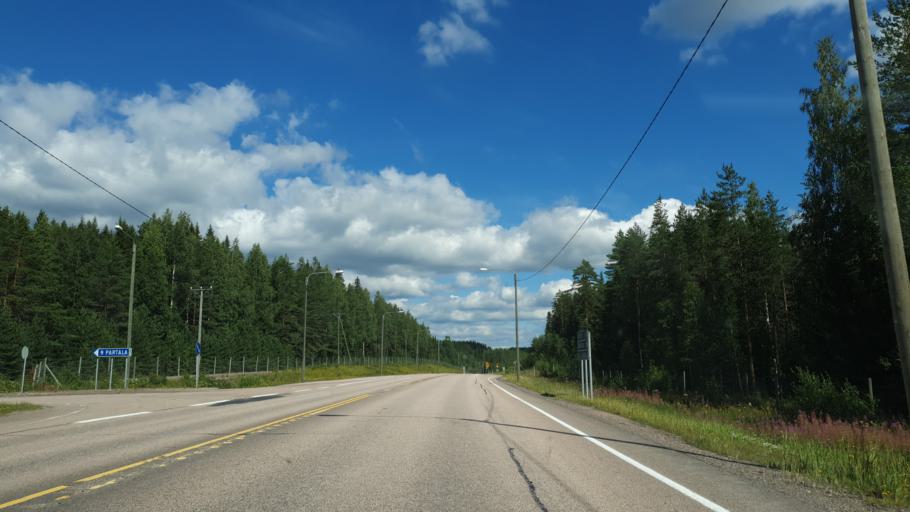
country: FI
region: Central Finland
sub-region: Jaemsae
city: Jaemsae
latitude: 61.7981
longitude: 24.9508
